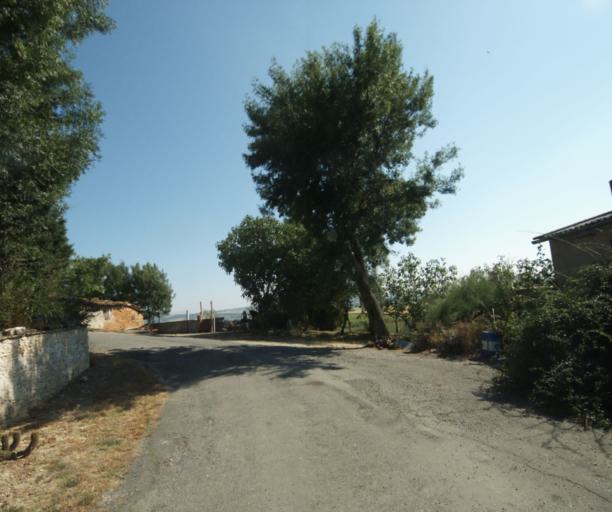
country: FR
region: Midi-Pyrenees
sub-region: Departement de la Haute-Garonne
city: Saint-Felix-Lauragais
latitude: 43.5154
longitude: 1.9369
